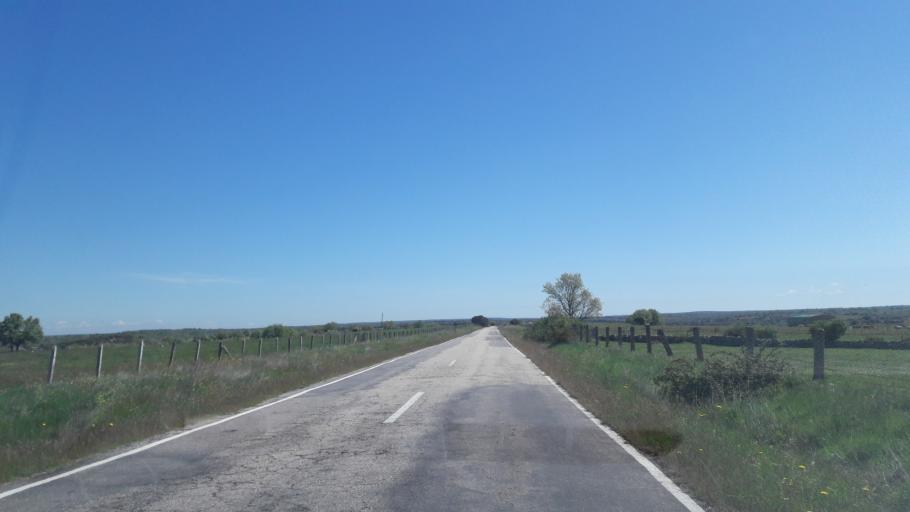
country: ES
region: Castille and Leon
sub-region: Provincia de Salamanca
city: Vitigudino
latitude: 41.0224
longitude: -6.4153
